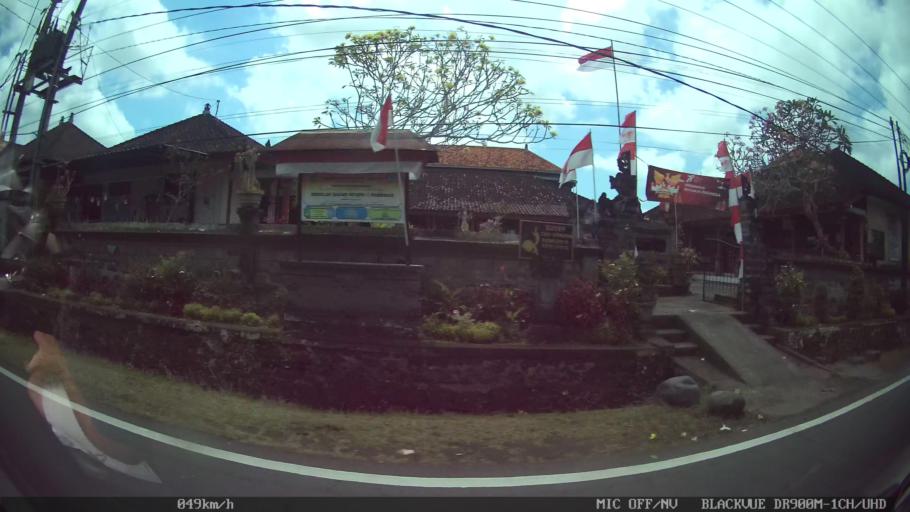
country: ID
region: Bali
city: Banjar Tebongkang
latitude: -8.5539
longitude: 115.2850
